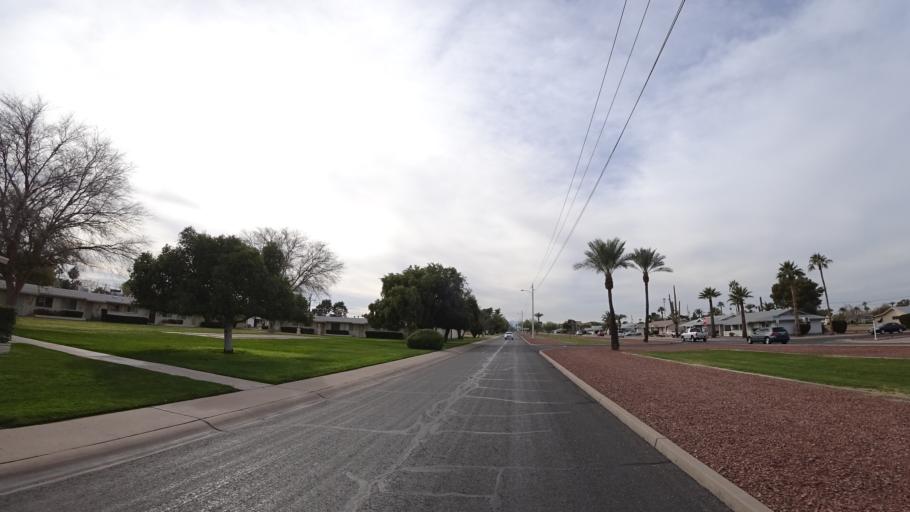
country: US
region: Arizona
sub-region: Maricopa County
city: Sun City
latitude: 33.5801
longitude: -112.2834
